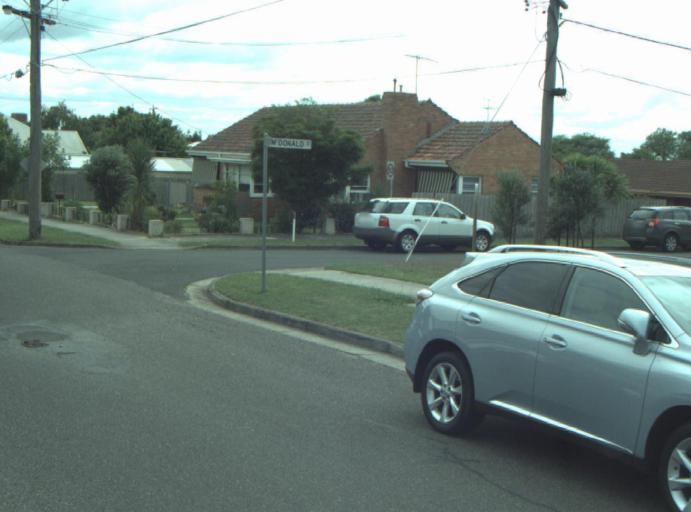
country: AU
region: Victoria
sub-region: Greater Geelong
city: Breakwater
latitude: -38.1717
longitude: 144.3425
